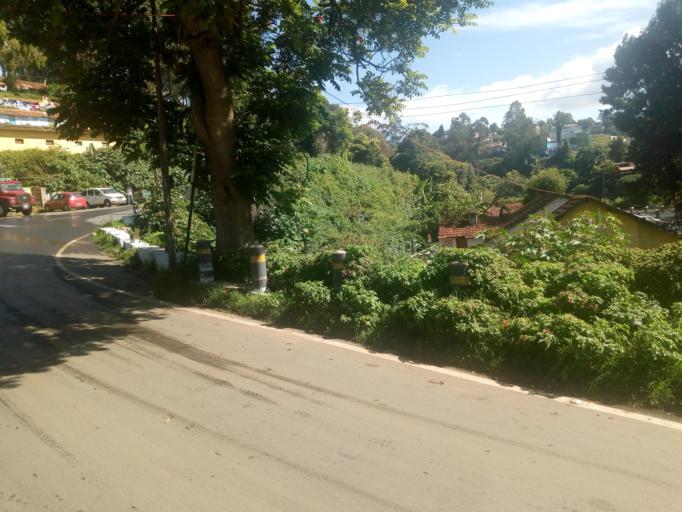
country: IN
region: Tamil Nadu
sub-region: Nilgiri
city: Wellington
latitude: 11.3440
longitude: 76.7907
